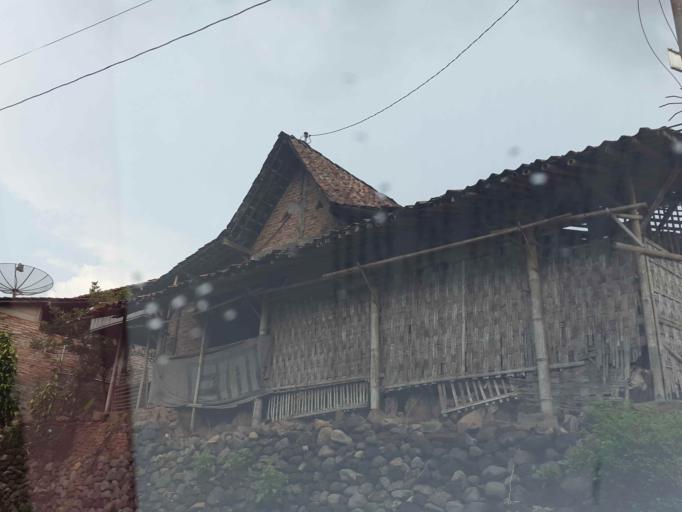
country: ID
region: Central Java
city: Magelang
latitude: -7.4189
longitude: 110.2502
